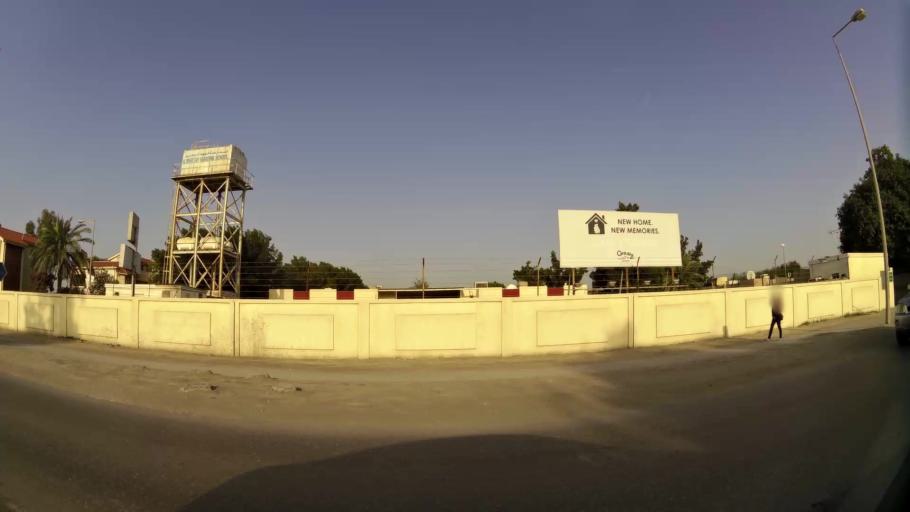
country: BH
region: Manama
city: Jidd Hafs
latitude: 26.1999
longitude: 50.4850
